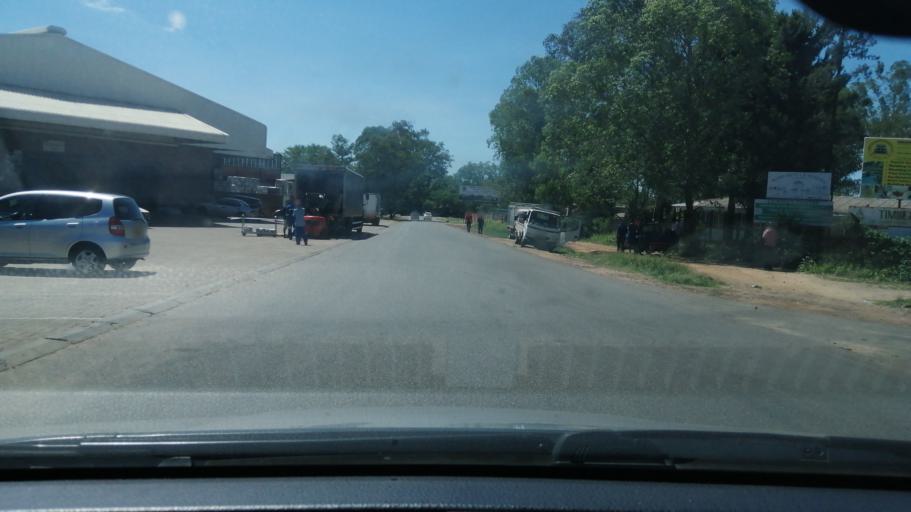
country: ZW
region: Harare
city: Epworth
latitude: -17.8399
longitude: 31.1197
